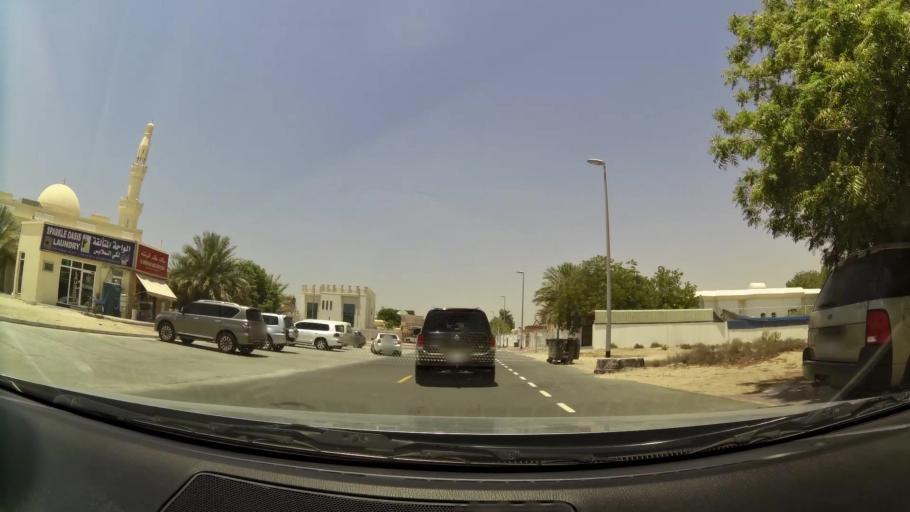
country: AE
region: Dubai
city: Dubai
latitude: 25.0893
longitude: 55.1946
